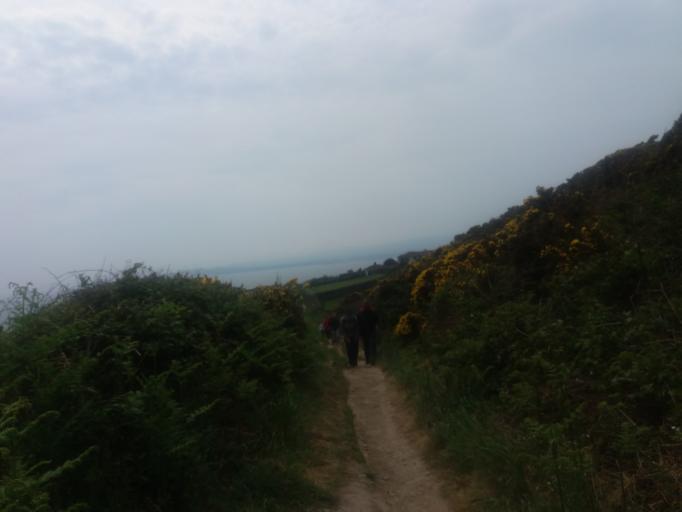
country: IE
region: Leinster
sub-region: Fingal County
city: Howth
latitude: 53.3682
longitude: -6.0548
